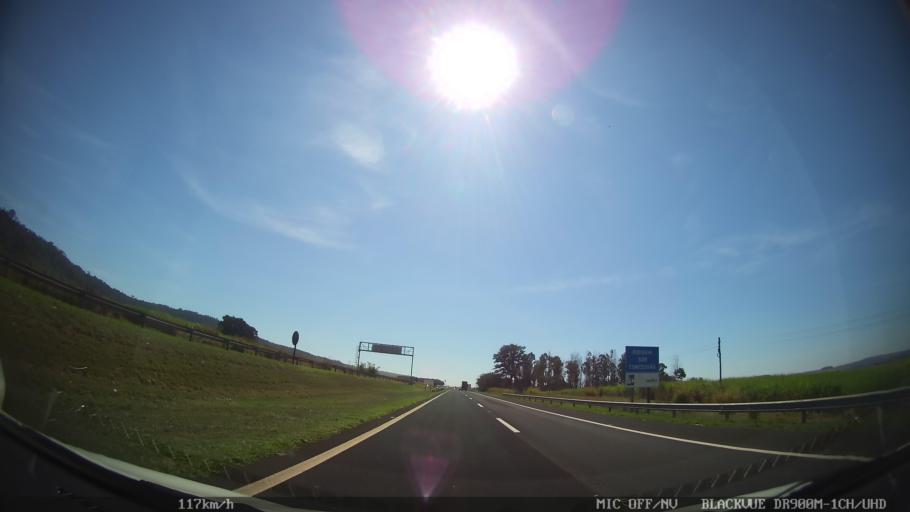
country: BR
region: Sao Paulo
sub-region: Sao Simao
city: Sao Simao
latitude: -21.5201
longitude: -47.6429
